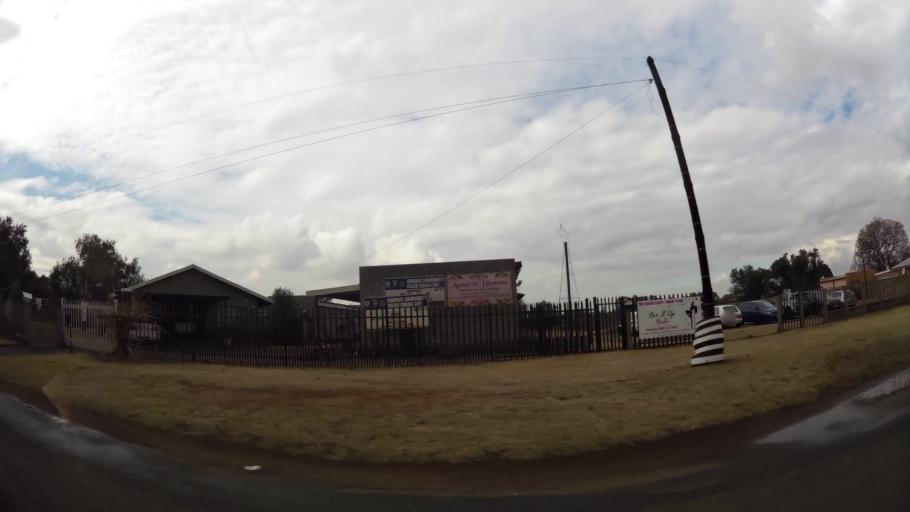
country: ZA
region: Gauteng
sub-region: Sedibeng District Municipality
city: Meyerton
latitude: -26.5797
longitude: 28.0036
